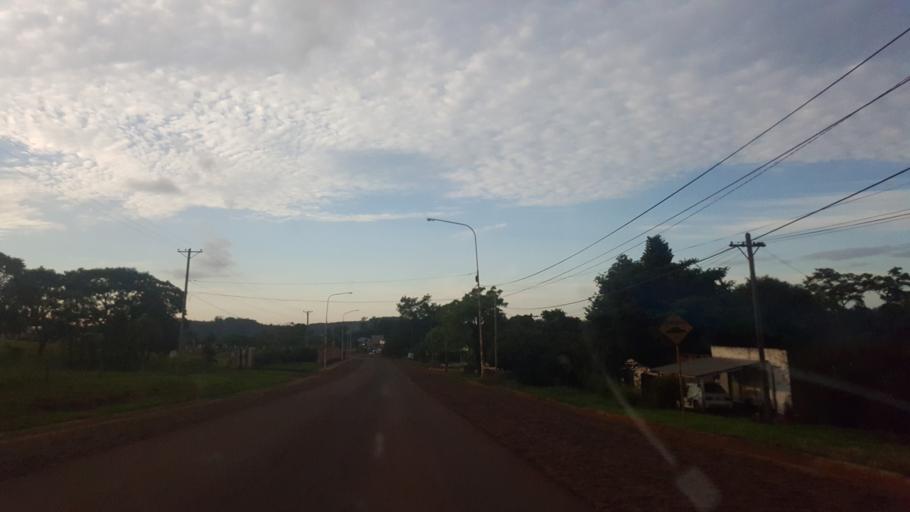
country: AR
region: Misiones
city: Dos de Mayo
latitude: -27.0331
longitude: -54.6856
